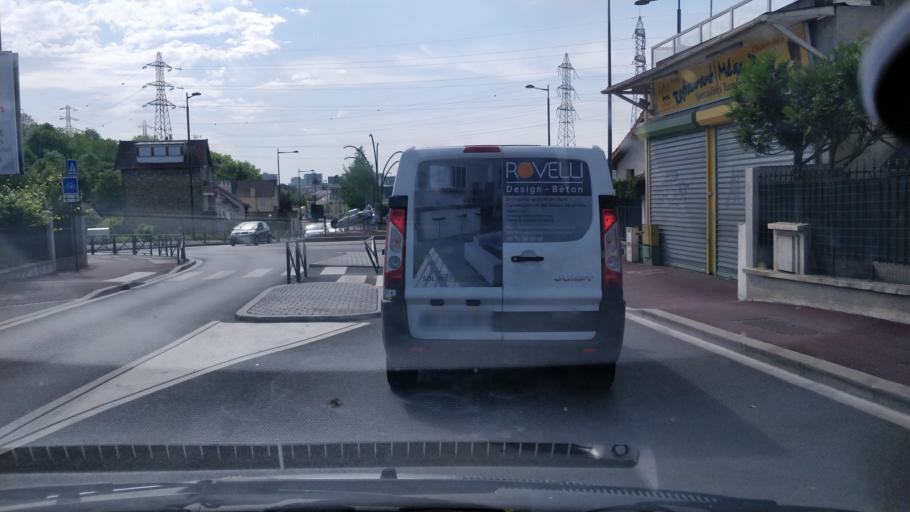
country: FR
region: Ile-de-France
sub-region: Departement de Seine-et-Marne
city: Chelles
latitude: 48.8871
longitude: 2.5849
